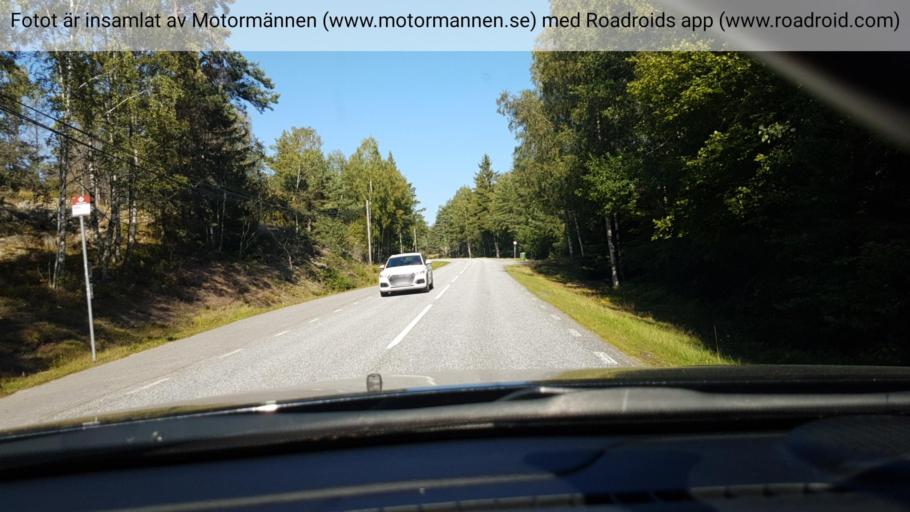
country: SE
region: Stockholm
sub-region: Haninge Kommun
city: Jordbro
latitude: 58.9896
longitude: 18.0983
